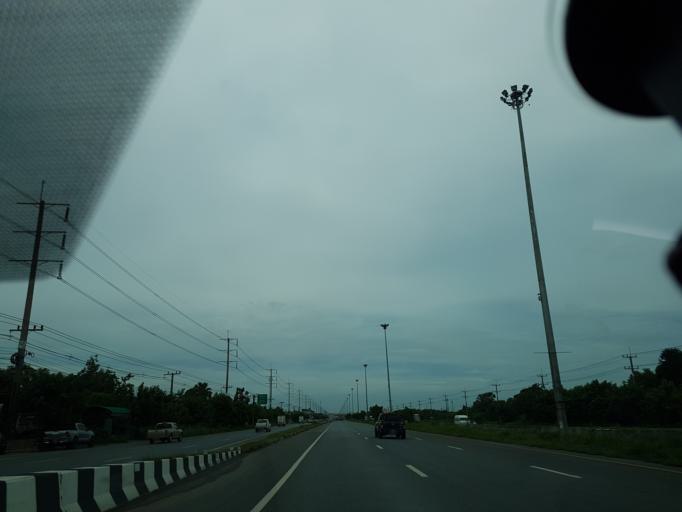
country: TH
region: Pathum Thani
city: Sam Khok
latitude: 14.0484
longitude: 100.5670
